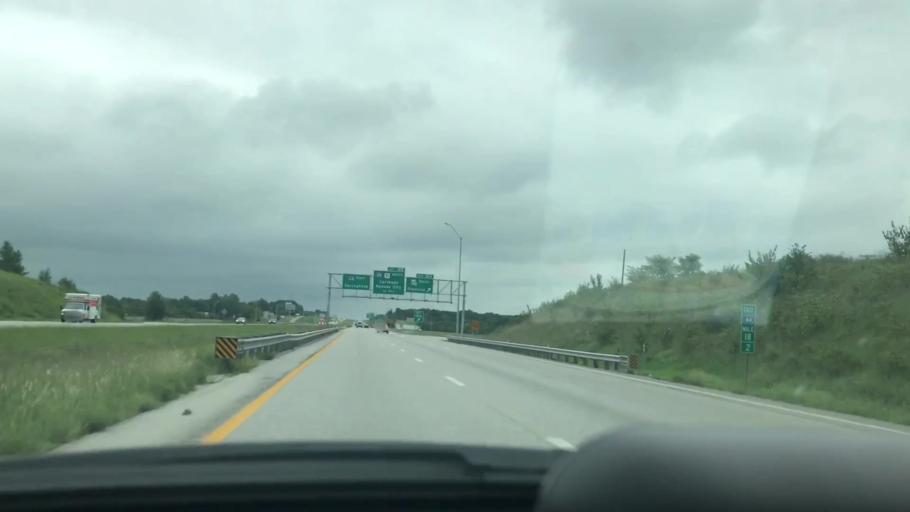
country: US
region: Missouri
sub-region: Jasper County
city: Carthage
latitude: 37.0818
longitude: -94.3178
